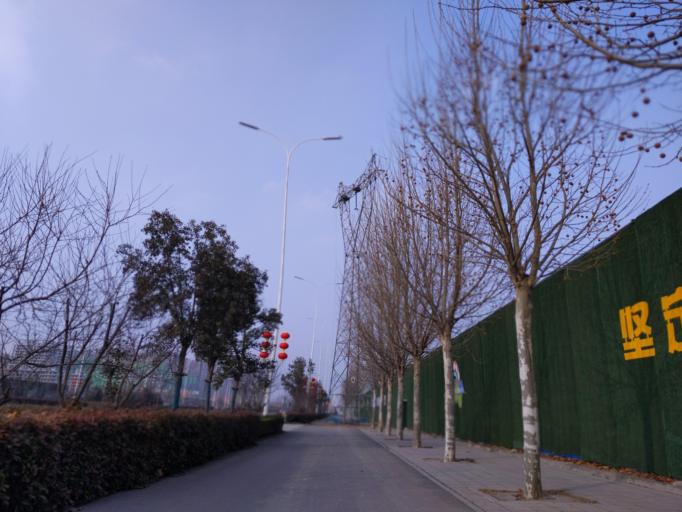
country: CN
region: Henan Sheng
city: Puyang
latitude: 35.8071
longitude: 115.0222
